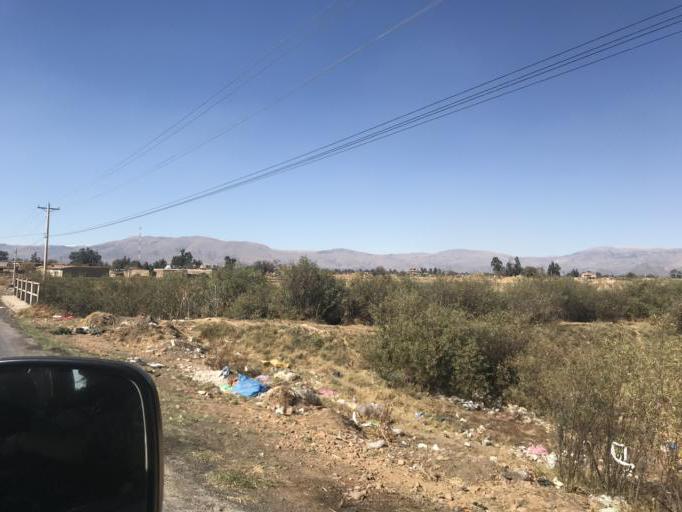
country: BO
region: Cochabamba
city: Cliza
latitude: -17.5688
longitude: -65.8940
